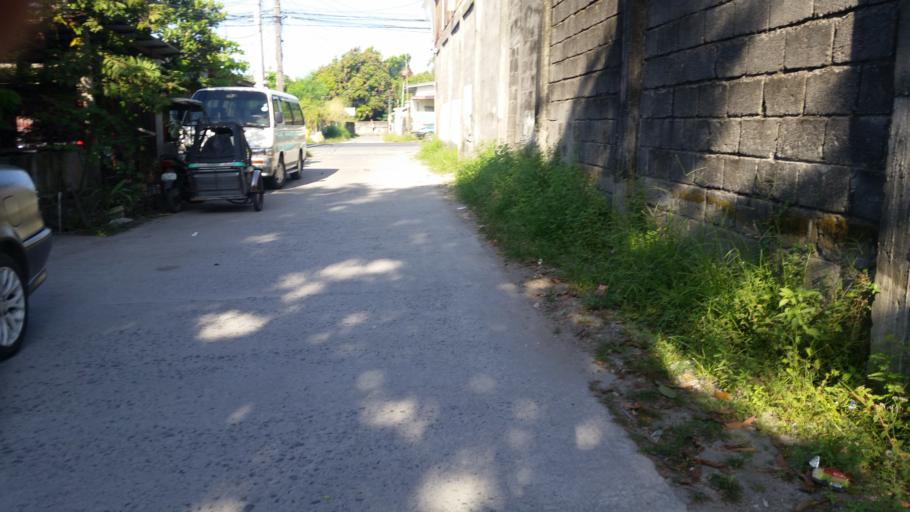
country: PH
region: Central Luzon
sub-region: Province of Pampanga
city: Mabalacat City
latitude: 15.2754
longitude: 120.5679
